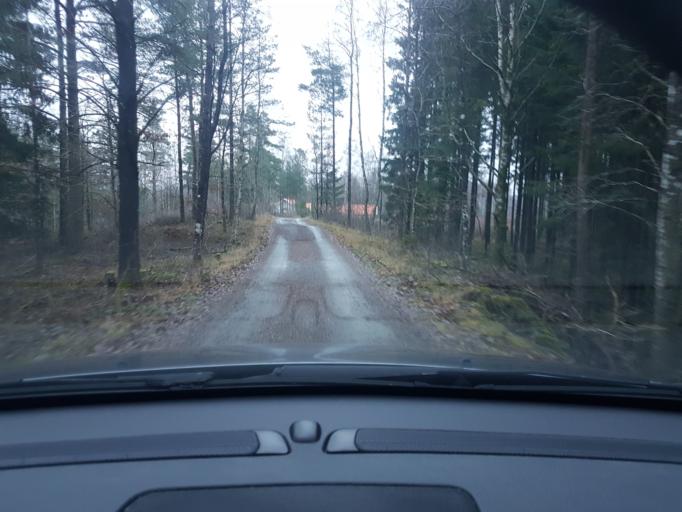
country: SE
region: Vaestra Goetaland
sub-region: Ale Kommun
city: Alvangen
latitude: 57.9559
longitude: 12.1374
